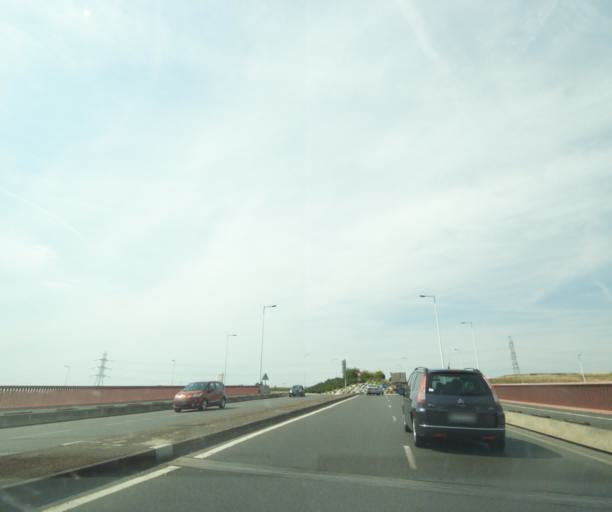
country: FR
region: Centre
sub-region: Departement d'Indre-et-Loire
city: Chambray-les-Tours
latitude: 47.3215
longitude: 0.7096
